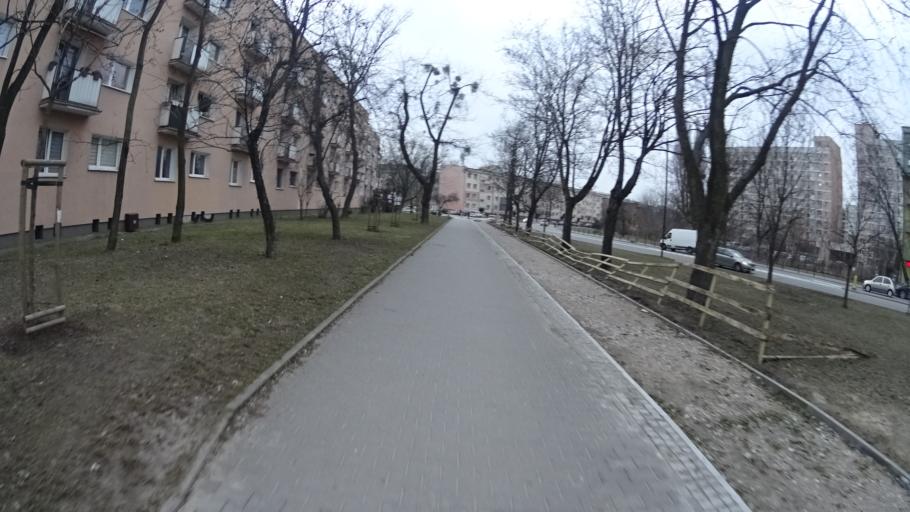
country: PL
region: Masovian Voivodeship
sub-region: Warszawa
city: Bemowo
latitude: 52.2386
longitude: 20.9435
